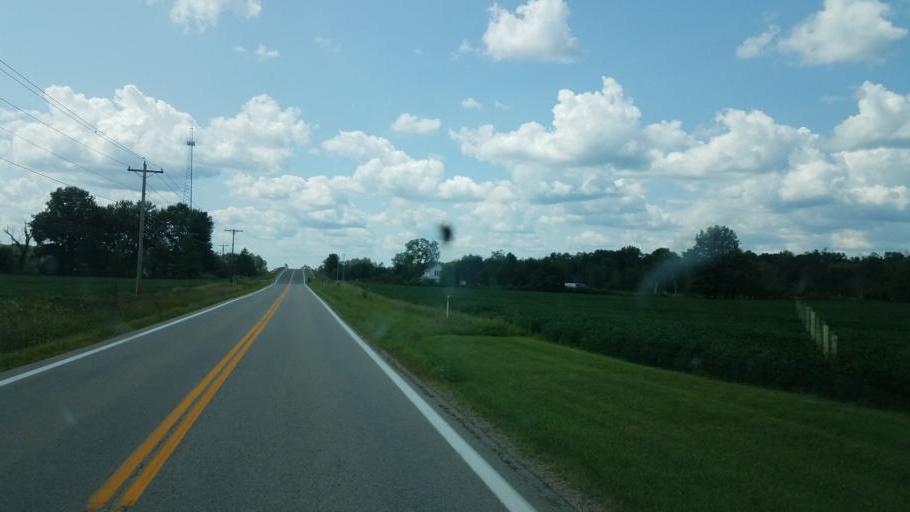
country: US
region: Ohio
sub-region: Delaware County
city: Sunbury
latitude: 40.3254
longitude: -82.8920
